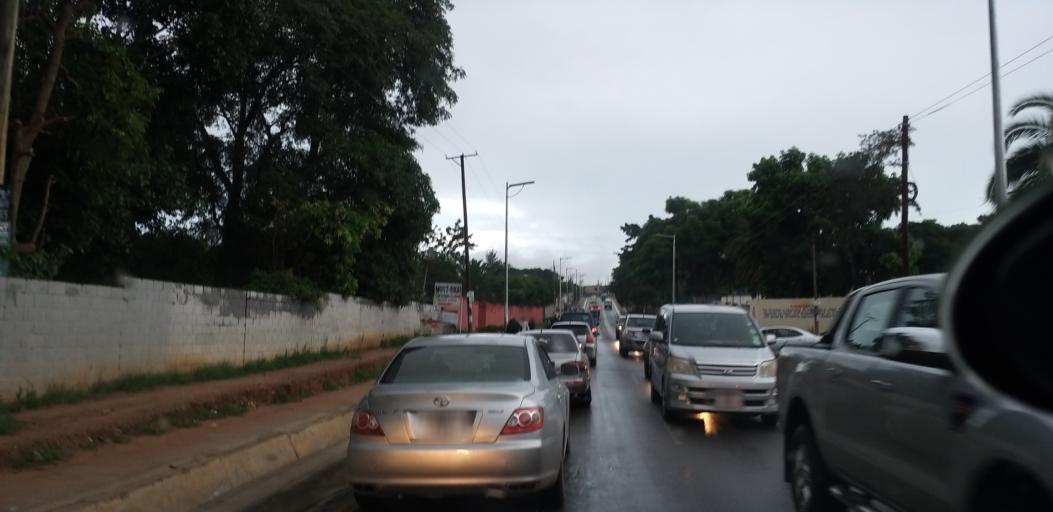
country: ZM
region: Lusaka
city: Lusaka
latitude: -15.4169
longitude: 28.3603
